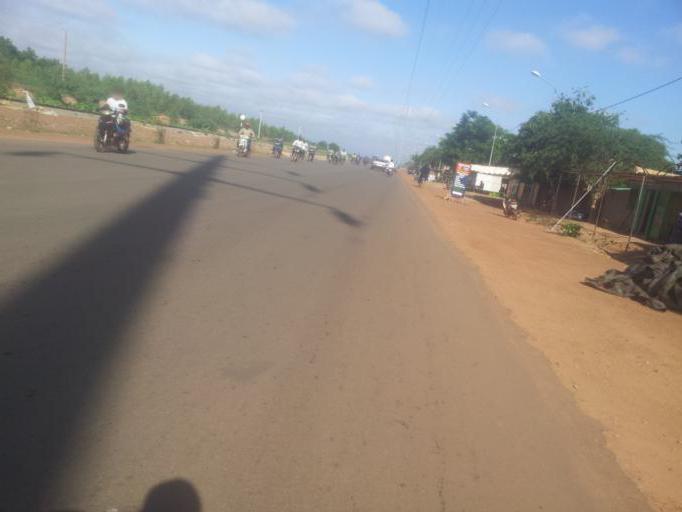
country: BF
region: Centre
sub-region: Kadiogo Province
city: Ouagadougou
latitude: 12.3701
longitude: -1.5602
